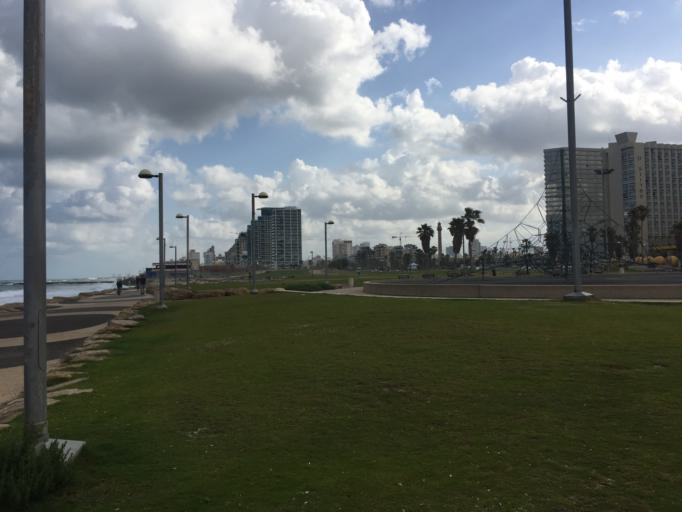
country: IL
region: Tel Aviv
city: Yafo
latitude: 32.0635
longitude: 34.7600
